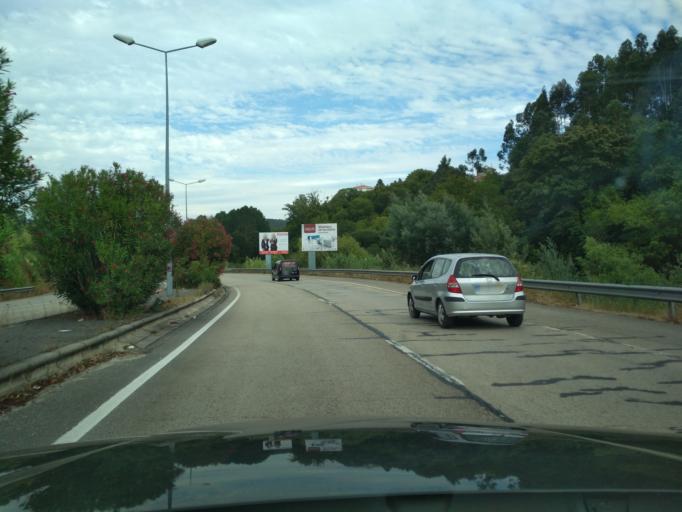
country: PT
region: Coimbra
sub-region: Coimbra
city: Coimbra
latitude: 40.2263
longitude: -8.4133
